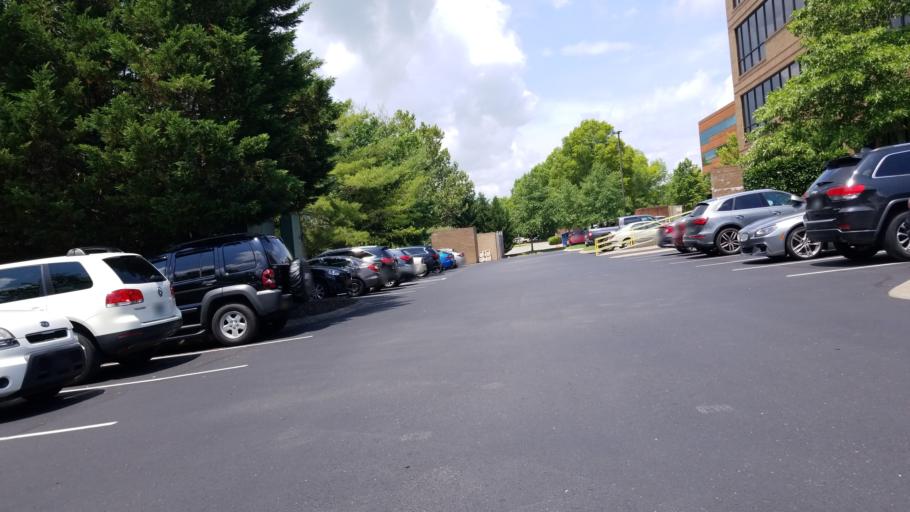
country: US
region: Tennessee
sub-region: Williamson County
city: Brentwood
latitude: 36.0368
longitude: -86.8058
